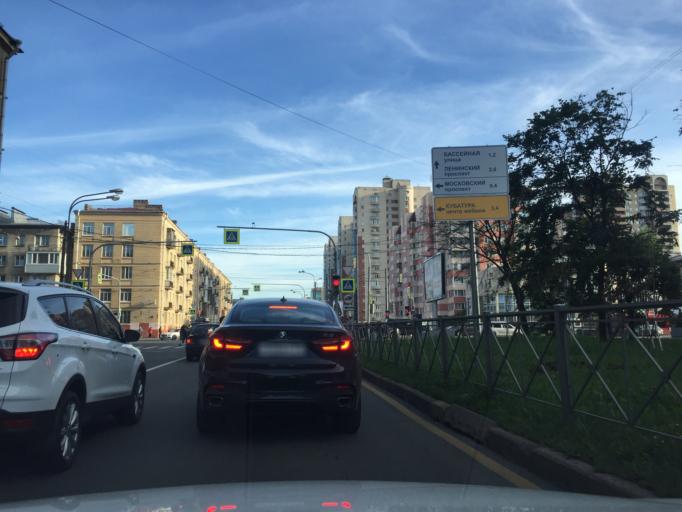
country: RU
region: St.-Petersburg
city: Admiralteisky
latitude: 59.8763
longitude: 30.3133
